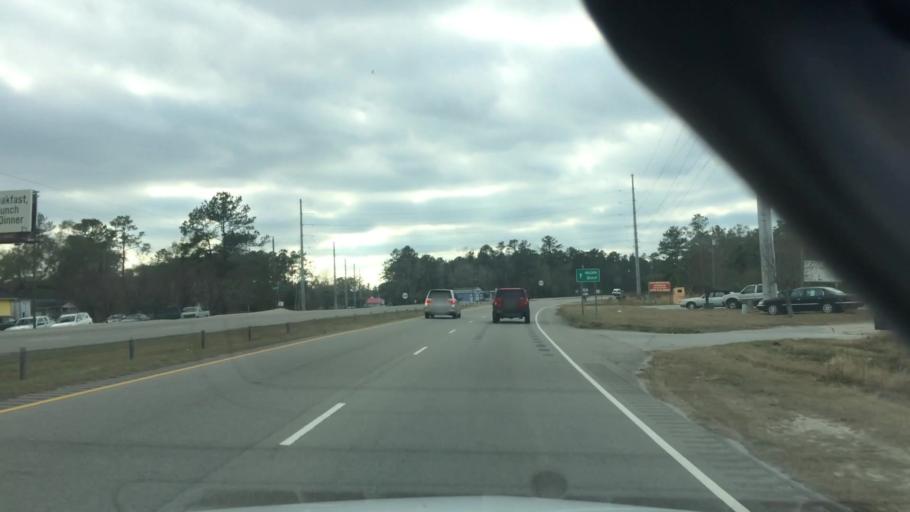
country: US
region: North Carolina
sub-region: Brunswick County
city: Bolivia
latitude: 34.0215
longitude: -78.2650
